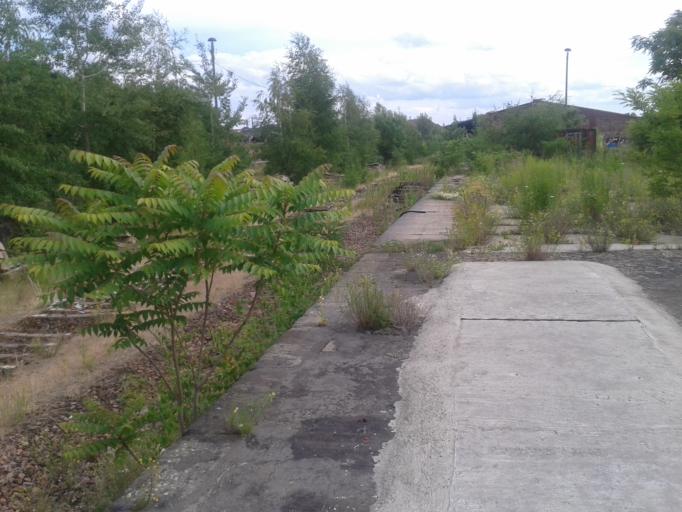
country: DE
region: Saxony
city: Dresden
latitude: 51.0676
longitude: 13.7367
